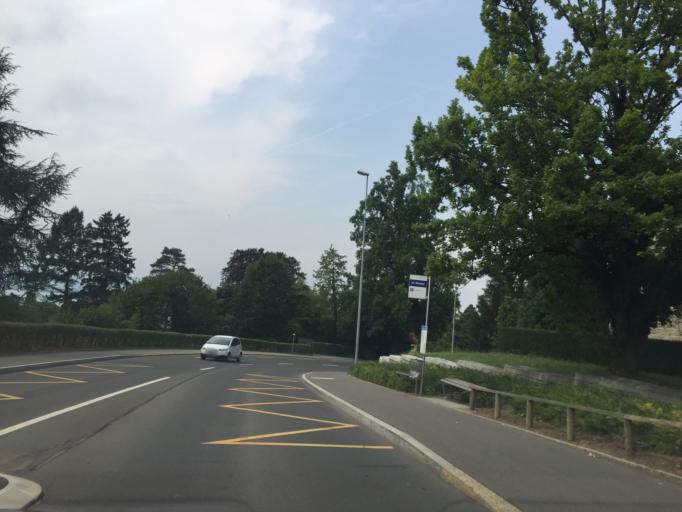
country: CH
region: Zug
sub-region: Zug
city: Zug
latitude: 47.1625
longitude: 8.5176
